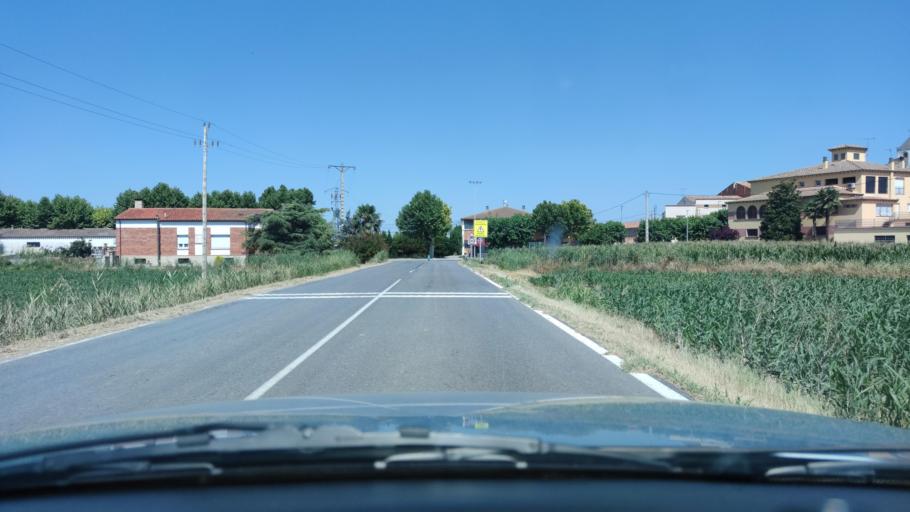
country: ES
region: Catalonia
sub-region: Provincia de Lleida
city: Linyola
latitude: 41.6956
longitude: 0.9518
